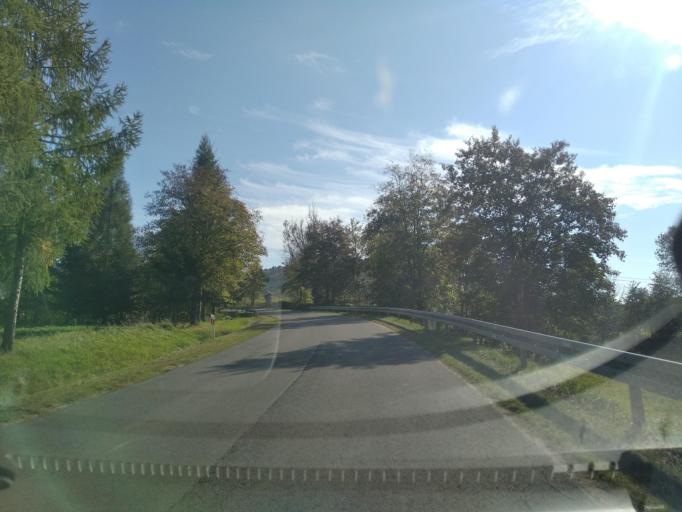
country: PL
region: Subcarpathian Voivodeship
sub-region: Powiat krosnienski
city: Jasliska
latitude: 49.4178
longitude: 21.9190
